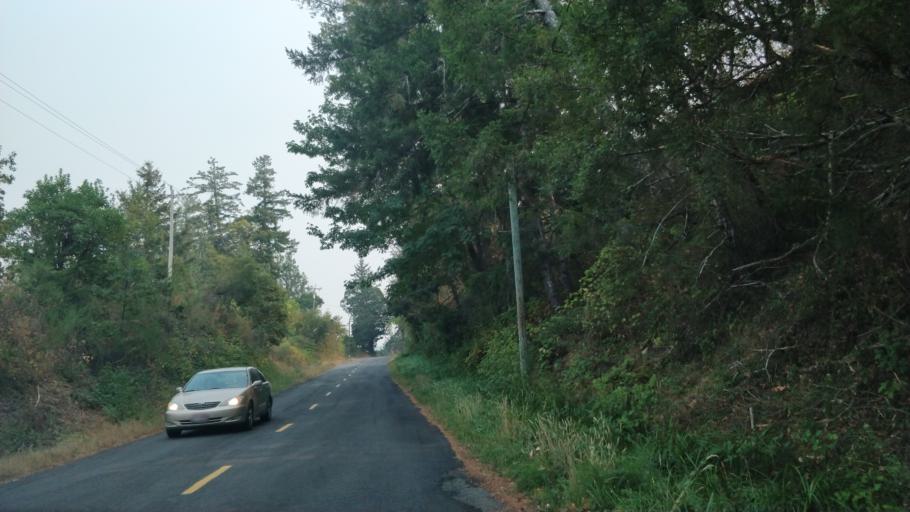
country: US
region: California
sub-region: Humboldt County
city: Rio Dell
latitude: 40.2400
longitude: -124.1638
